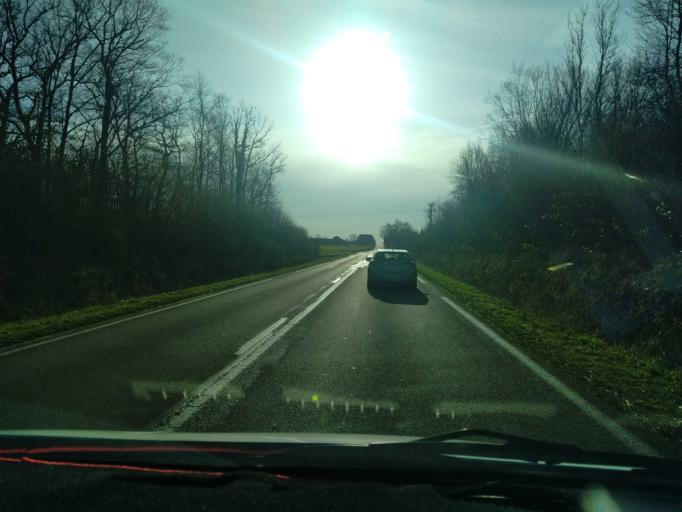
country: FR
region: Franche-Comte
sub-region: Departement de la Haute-Saone
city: Gray
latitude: 47.3782
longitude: 5.6619
